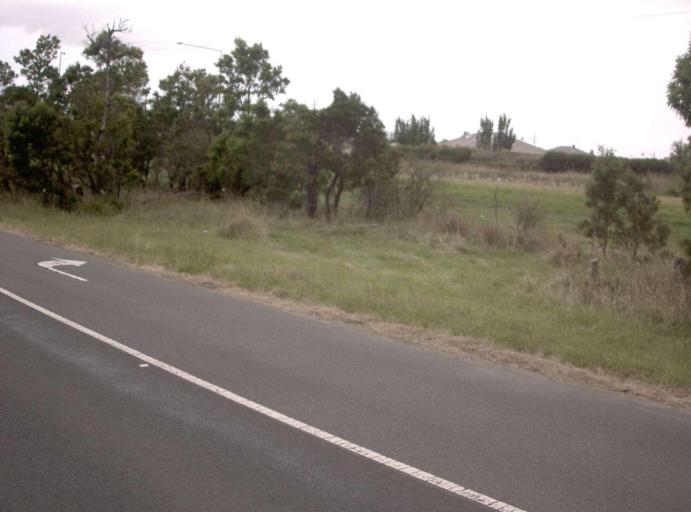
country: AU
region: Victoria
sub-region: Cardinia
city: Officer
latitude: -38.0616
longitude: 145.4414
